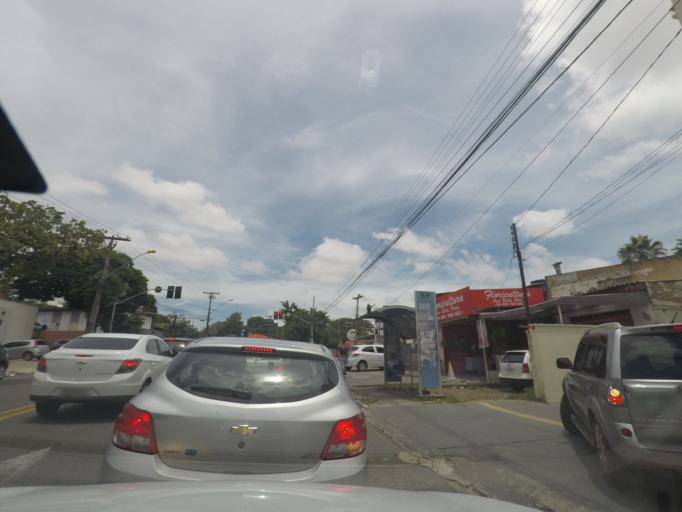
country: BR
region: Goias
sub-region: Goiania
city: Goiania
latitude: -16.6891
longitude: -49.2518
